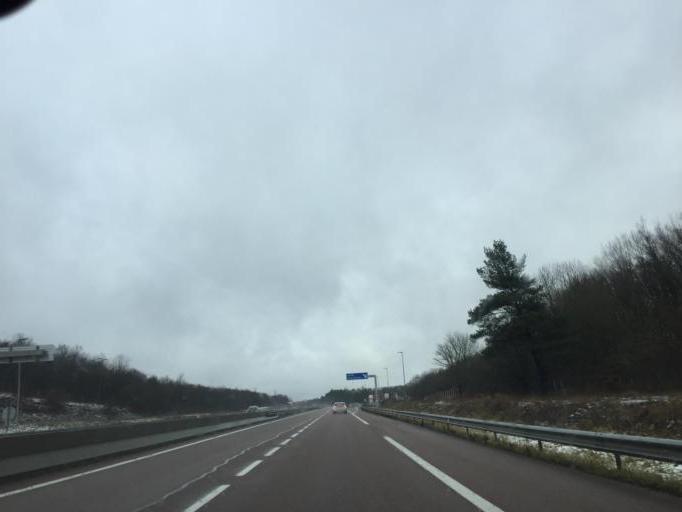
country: FR
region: Bourgogne
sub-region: Departement de la Cote-d'Or
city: Savigny-les-Beaune
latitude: 47.1079
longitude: 4.7136
